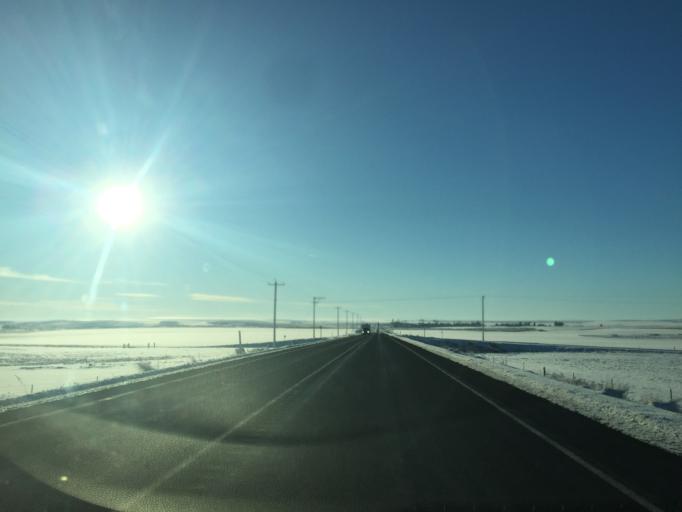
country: US
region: Washington
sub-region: Okanogan County
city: Coulee Dam
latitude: 47.7219
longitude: -118.8934
